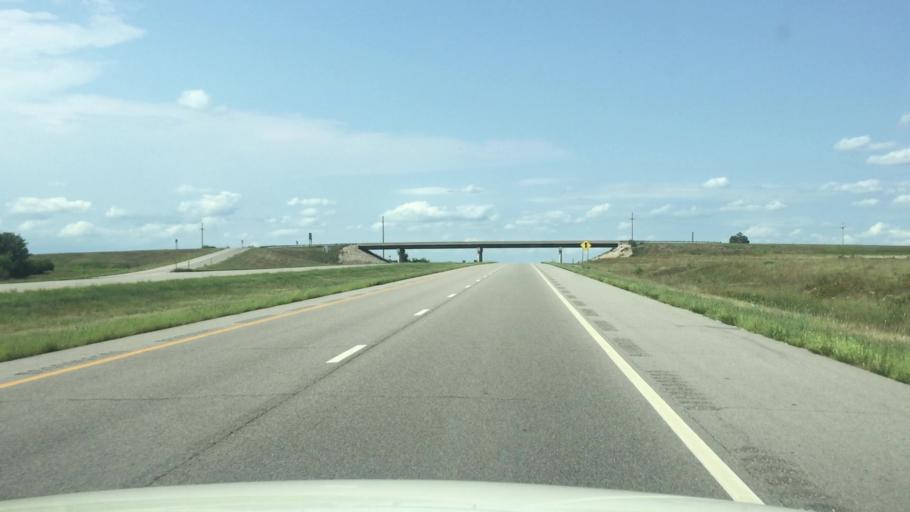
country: US
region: Kansas
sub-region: Linn County
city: La Cygne
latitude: 38.4003
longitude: -94.6877
